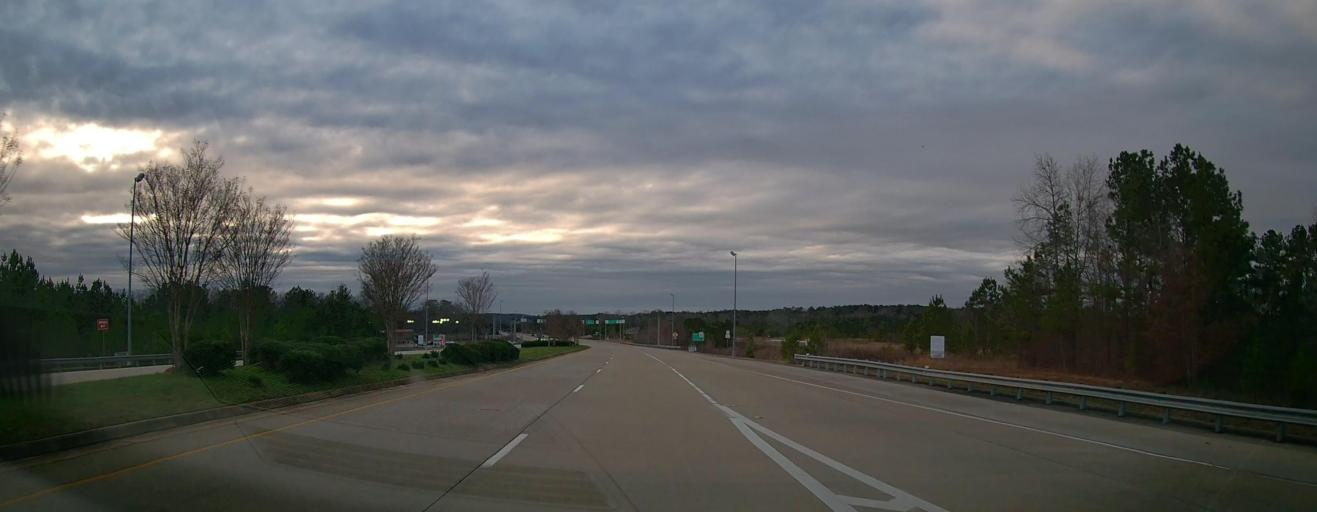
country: US
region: Georgia
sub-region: Troup County
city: West Point
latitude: 32.9290
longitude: -85.1109
